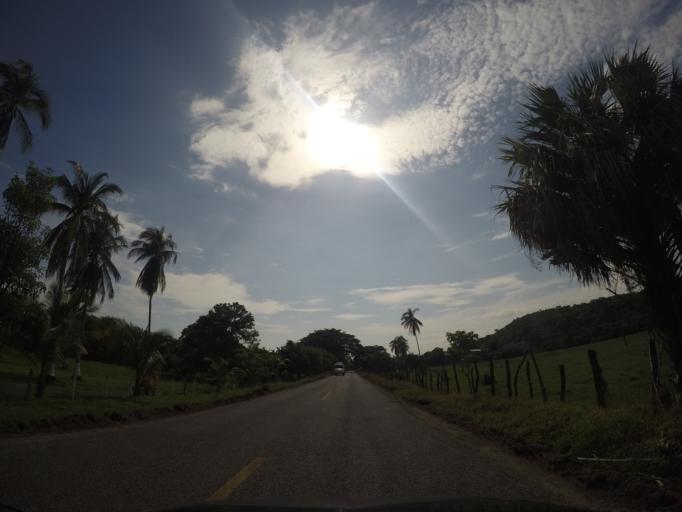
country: MX
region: Oaxaca
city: San Pedro Mixtepec
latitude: 15.9396
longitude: -97.1702
